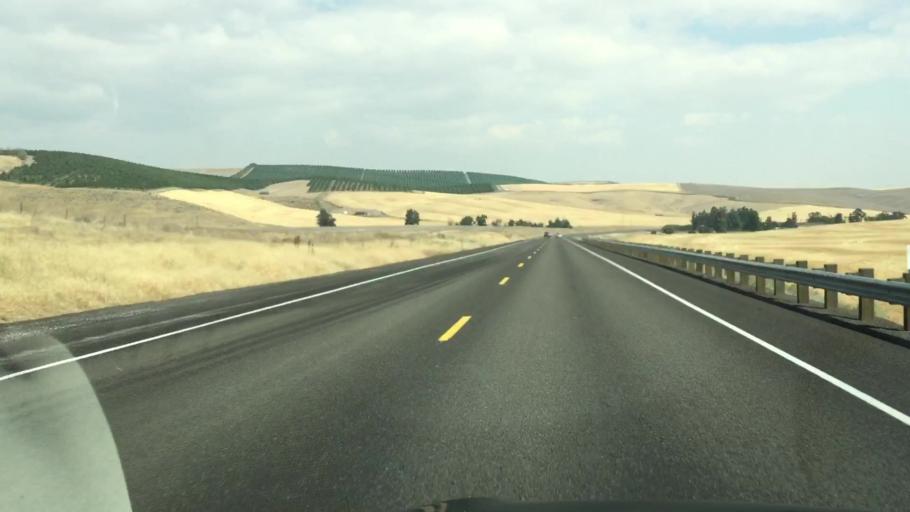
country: US
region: Oregon
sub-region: Wasco County
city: The Dalles
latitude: 45.4780
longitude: -121.1173
